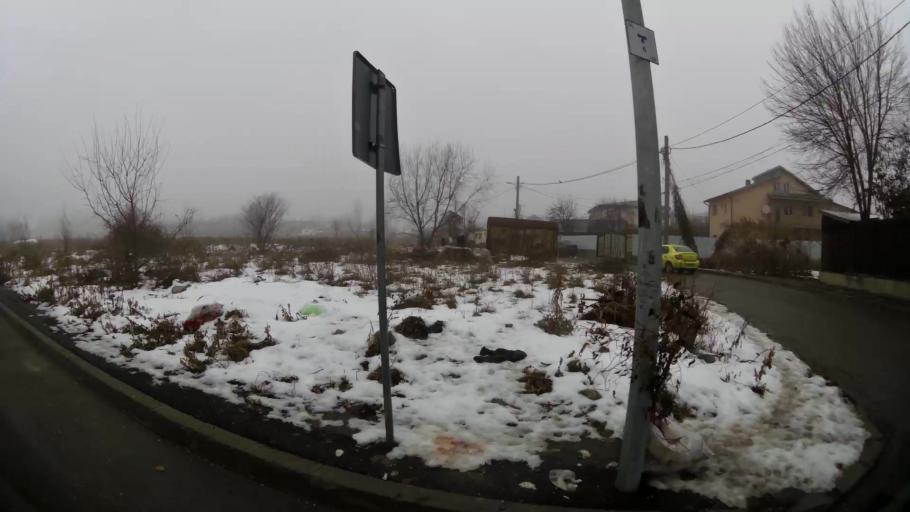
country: RO
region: Ilfov
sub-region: Comuna Chiajna
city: Rosu
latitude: 44.4704
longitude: 26.0145
